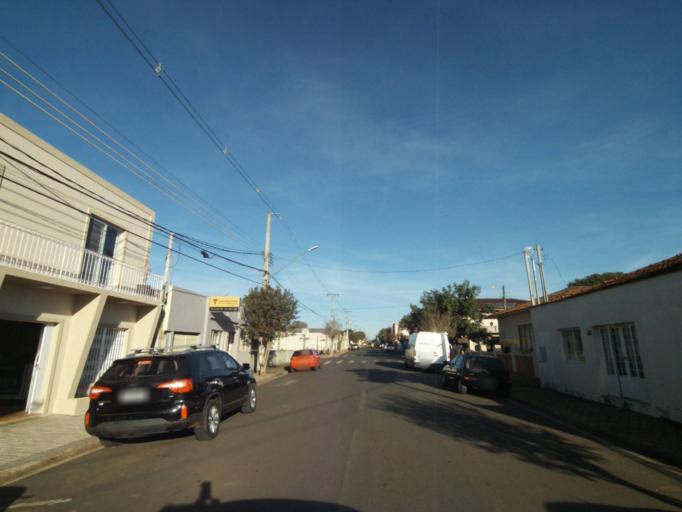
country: BR
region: Parana
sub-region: Tibagi
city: Tibagi
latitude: -24.5129
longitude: -50.4113
